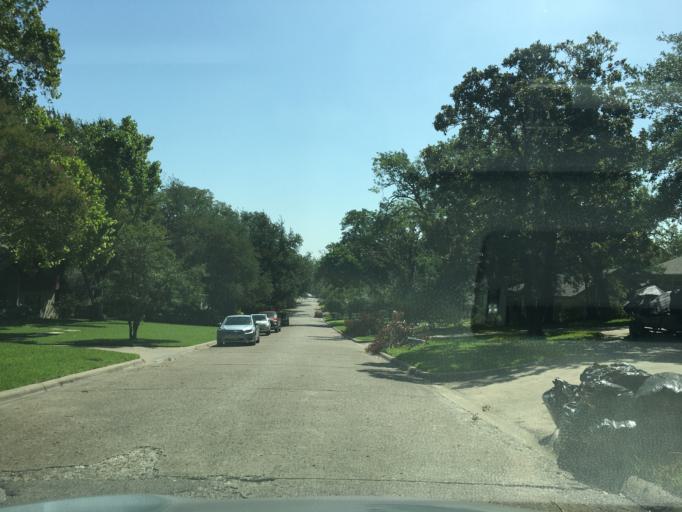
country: US
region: Texas
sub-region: Dallas County
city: University Park
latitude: 32.9051
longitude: -96.7756
